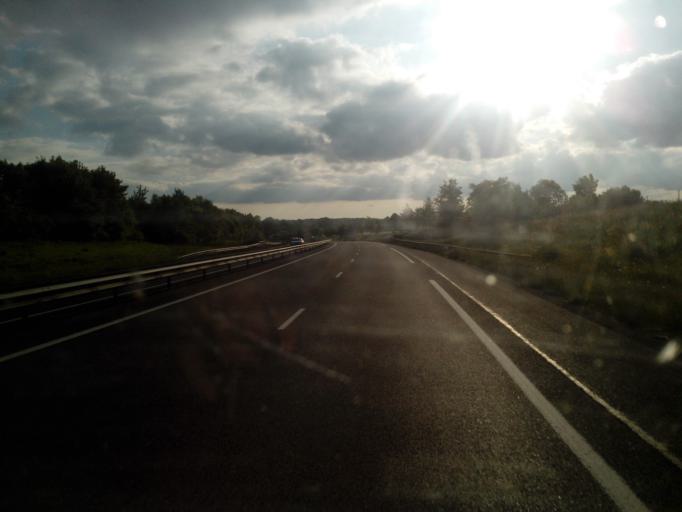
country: FR
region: Lower Normandy
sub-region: Departement du Calvados
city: Saint-Martin-des-Besaces
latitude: 49.0151
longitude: -0.8676
